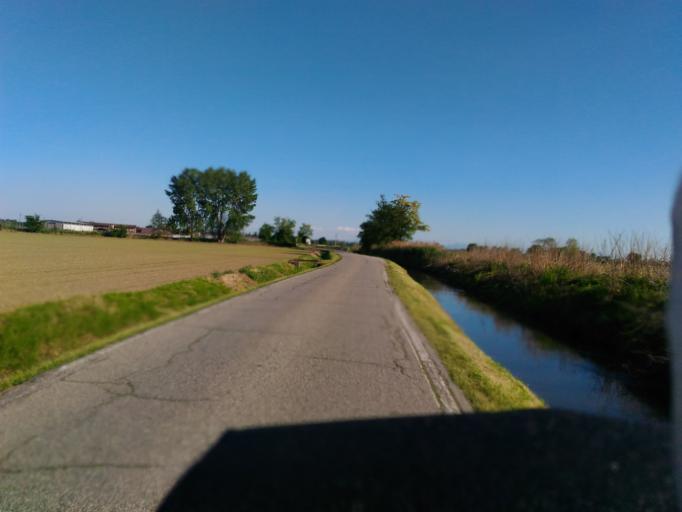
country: IT
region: Lombardy
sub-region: Citta metropolitana di Milano
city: Locate di Triulzi
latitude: 45.3641
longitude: 9.2484
